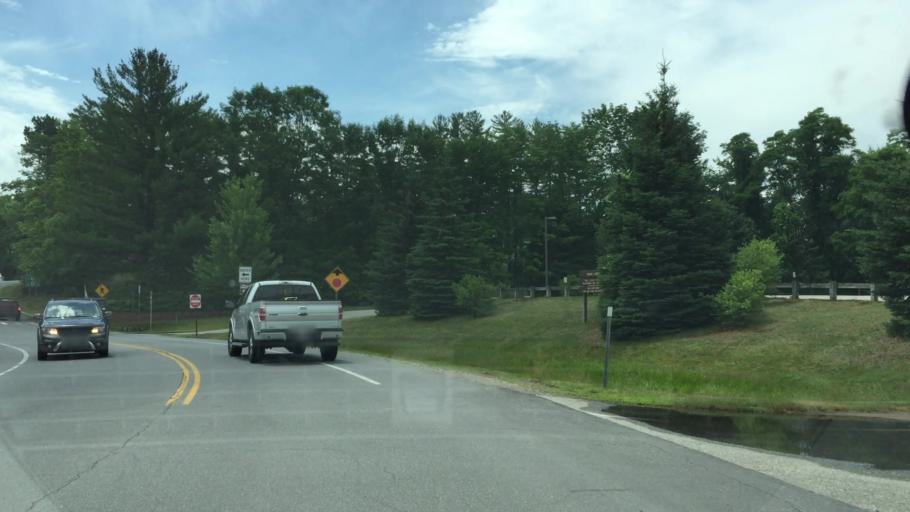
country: US
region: New Hampshire
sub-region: Grafton County
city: Holderness
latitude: 43.7327
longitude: -71.5883
